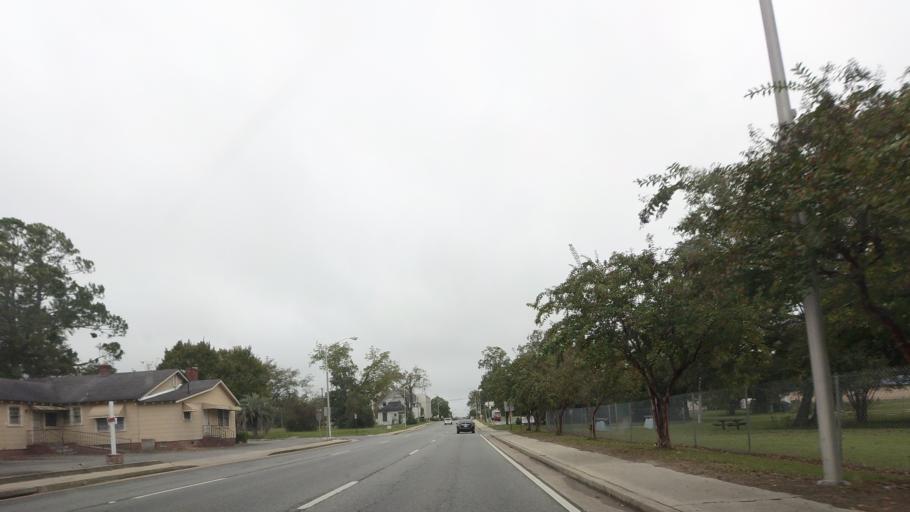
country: US
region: Georgia
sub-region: Ben Hill County
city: Fitzgerald
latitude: 31.7098
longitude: -83.2515
